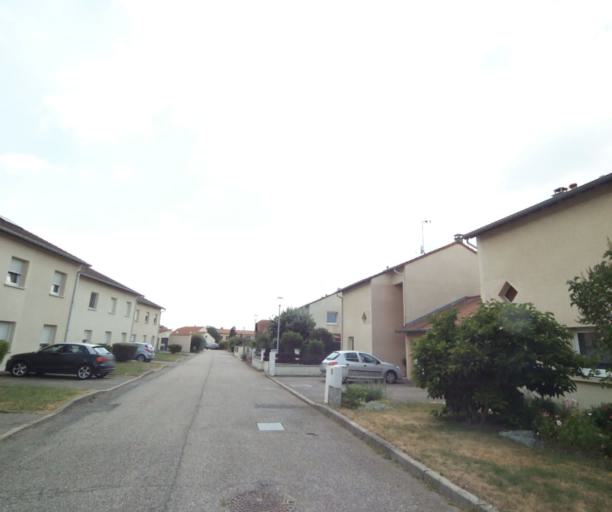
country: FR
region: Lorraine
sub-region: Departement de Meurthe-et-Moselle
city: Luneville
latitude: 48.5918
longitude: 6.4845
